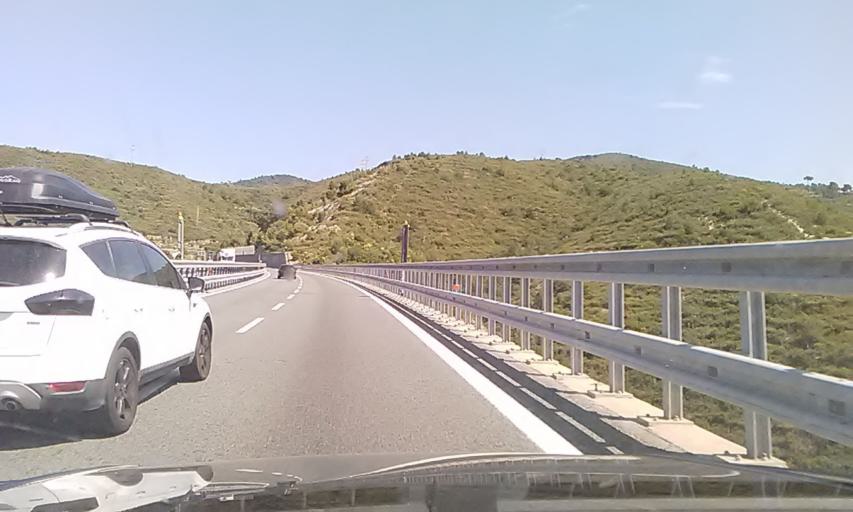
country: IT
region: Liguria
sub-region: Provincia di Savona
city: Laigueglia
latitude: 43.9934
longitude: 8.1368
